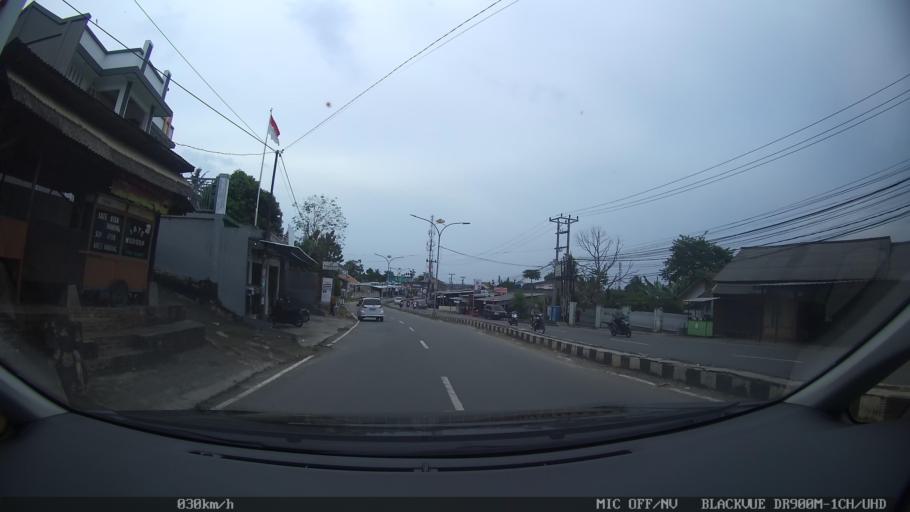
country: ID
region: Lampung
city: Kedaton
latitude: -5.3795
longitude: 105.2216
